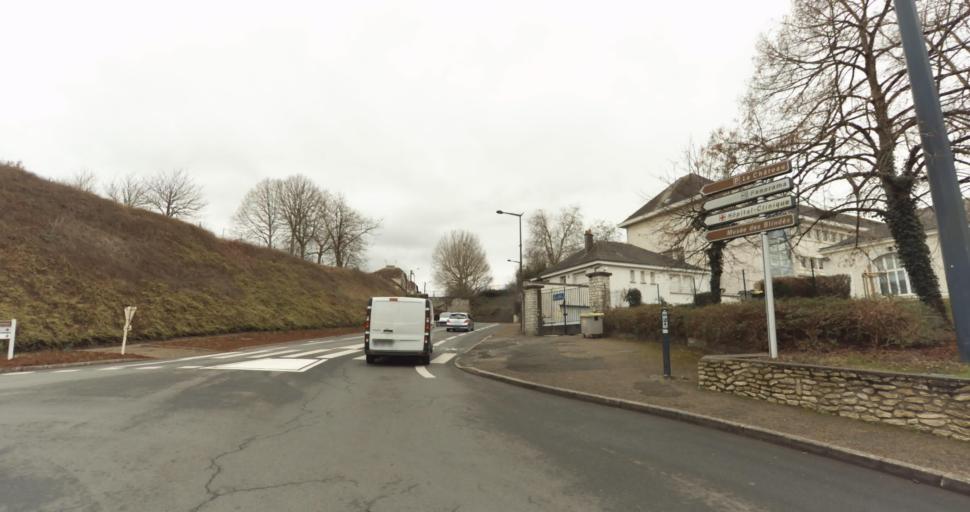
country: FR
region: Pays de la Loire
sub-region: Departement de Maine-et-Loire
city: Saumur
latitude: 47.2554
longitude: -0.0738
